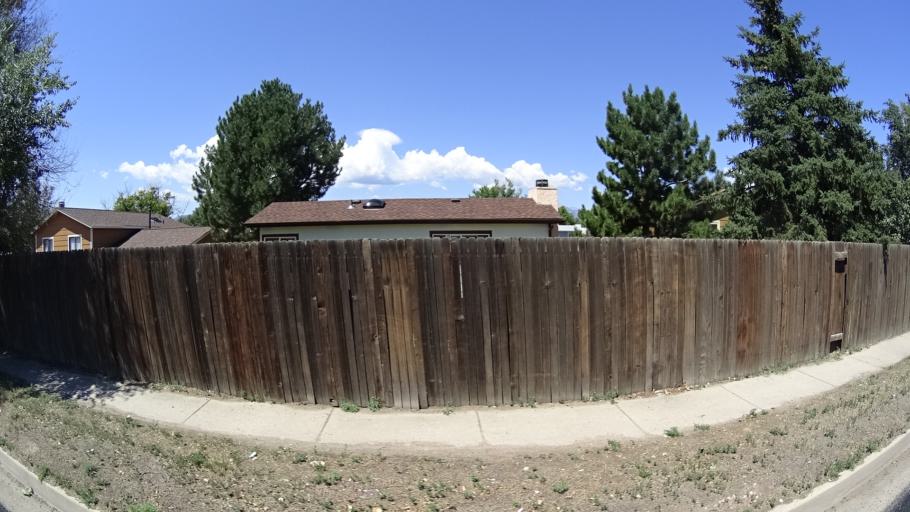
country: US
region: Colorado
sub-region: El Paso County
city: Stratmoor
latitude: 38.7834
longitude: -104.7390
